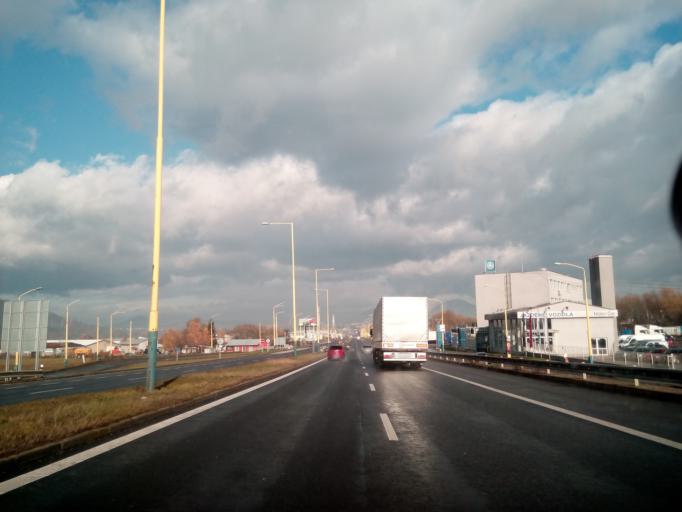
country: SK
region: Presovsky
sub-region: Okres Presov
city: Presov
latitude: 48.9591
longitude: 21.2567
